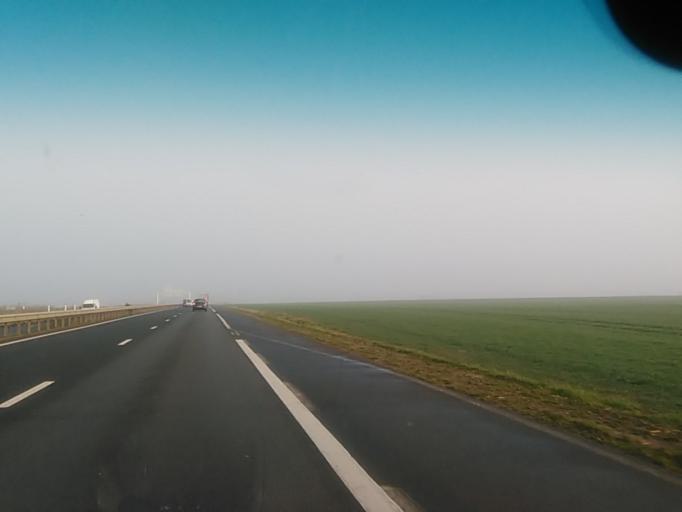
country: FR
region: Lower Normandy
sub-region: Departement du Calvados
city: Bourguebus
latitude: 49.1057
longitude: -0.3159
